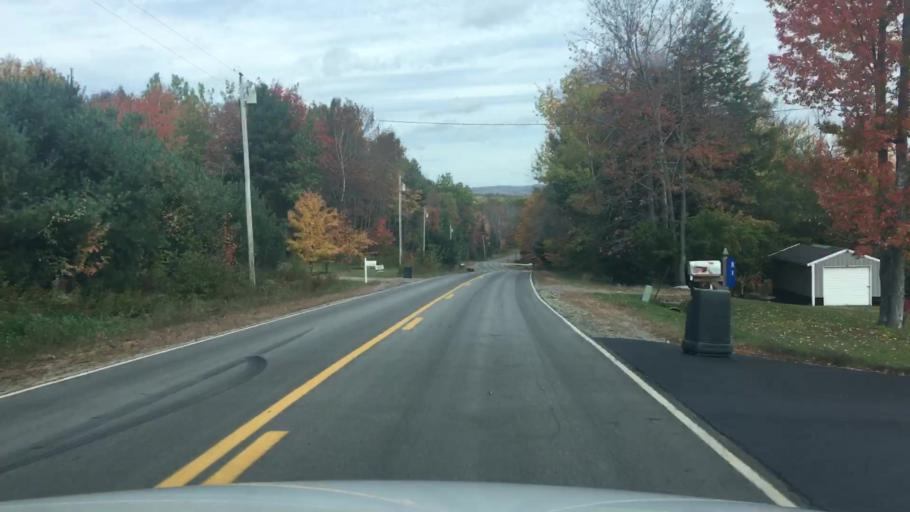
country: US
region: Maine
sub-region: Waldo County
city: Searsmont
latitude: 44.4023
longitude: -69.1372
